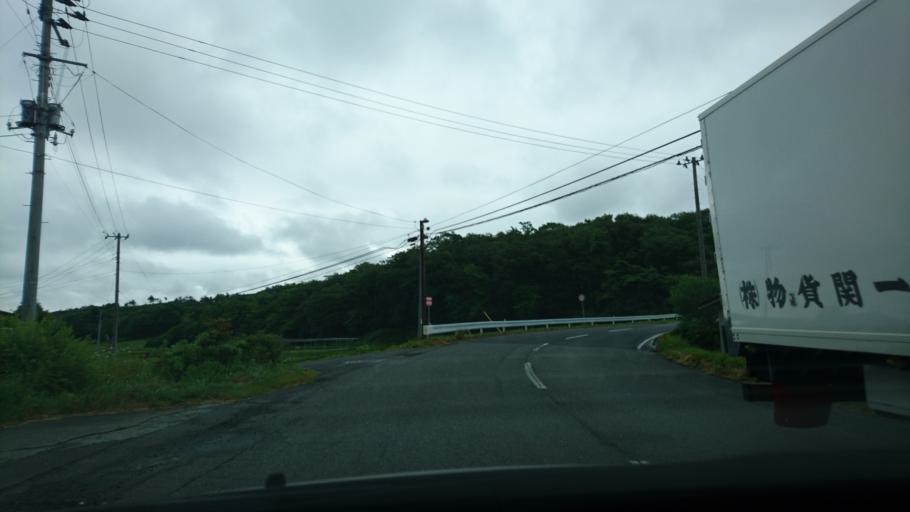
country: JP
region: Iwate
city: Ichinoseki
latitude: 38.8868
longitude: 141.1448
